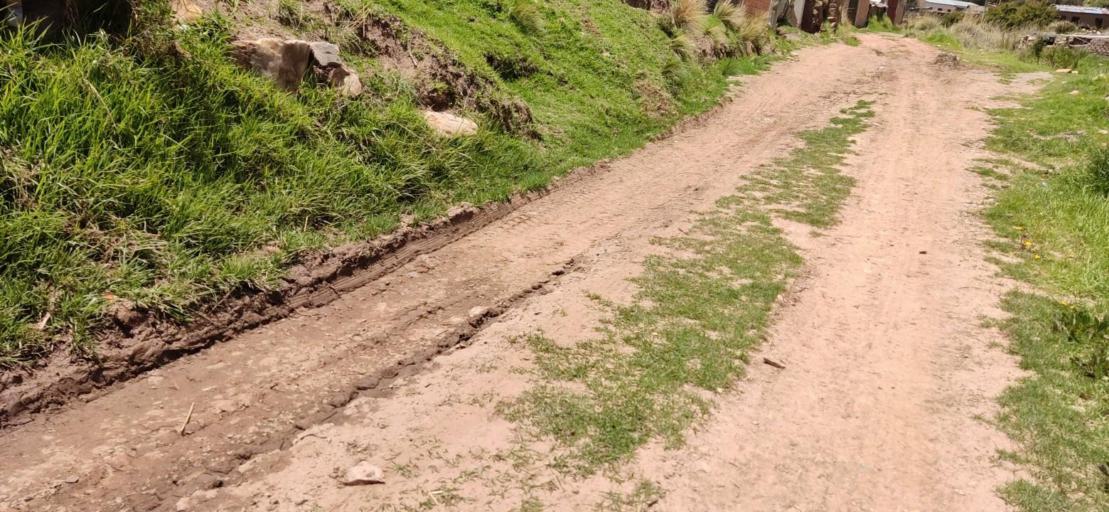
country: BO
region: La Paz
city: Batallas
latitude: -16.3465
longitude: -68.6398
